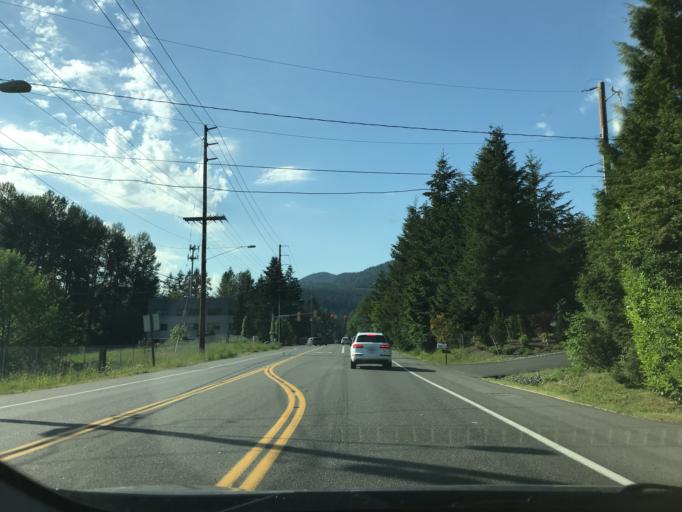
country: US
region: Washington
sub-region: King County
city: Mirrormont
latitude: 47.4717
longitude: -122.0223
